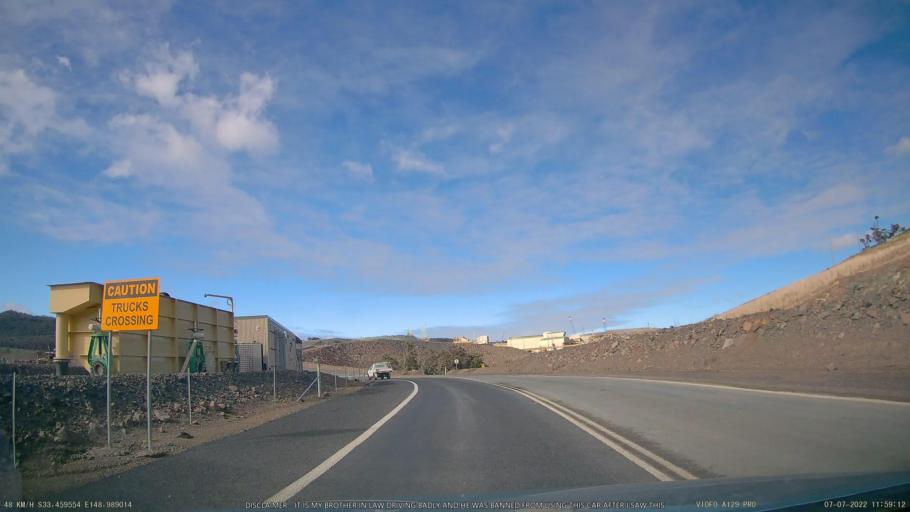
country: AU
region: New South Wales
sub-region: Blayney
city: Millthorpe
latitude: -33.4599
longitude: 148.9893
